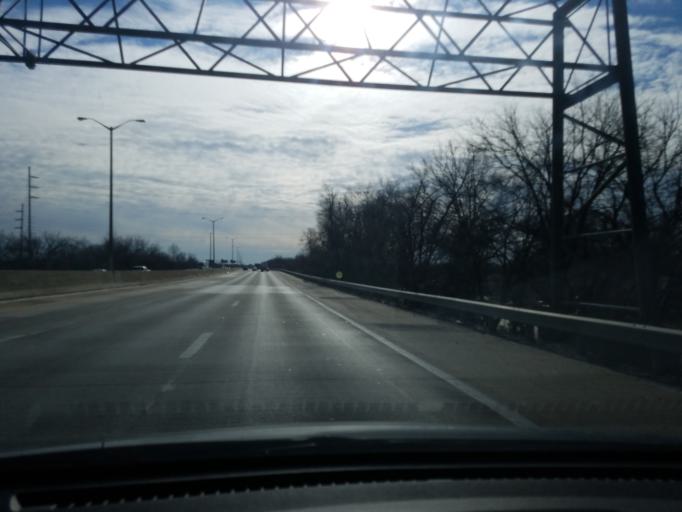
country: US
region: Kentucky
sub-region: Jefferson County
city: Shively
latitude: 38.2247
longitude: -85.8221
